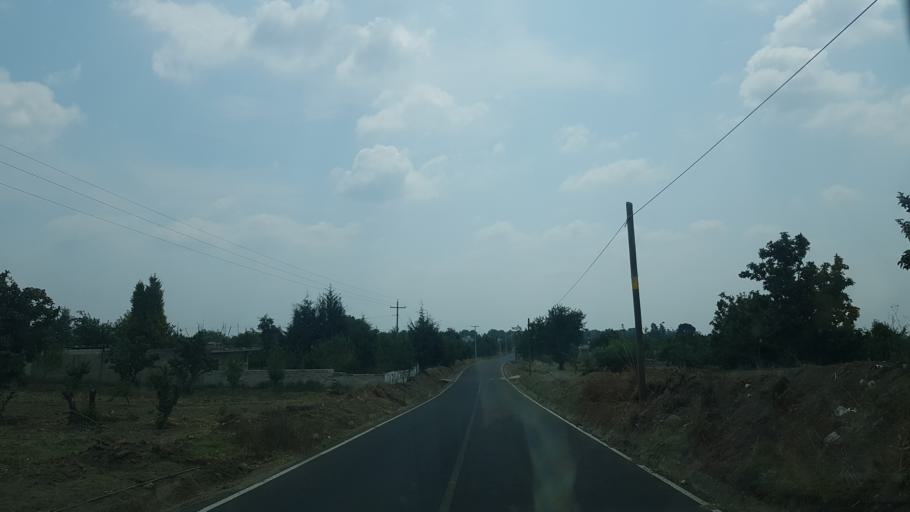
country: MX
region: Puebla
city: Domingo Arenas
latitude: 19.1420
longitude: -98.4758
